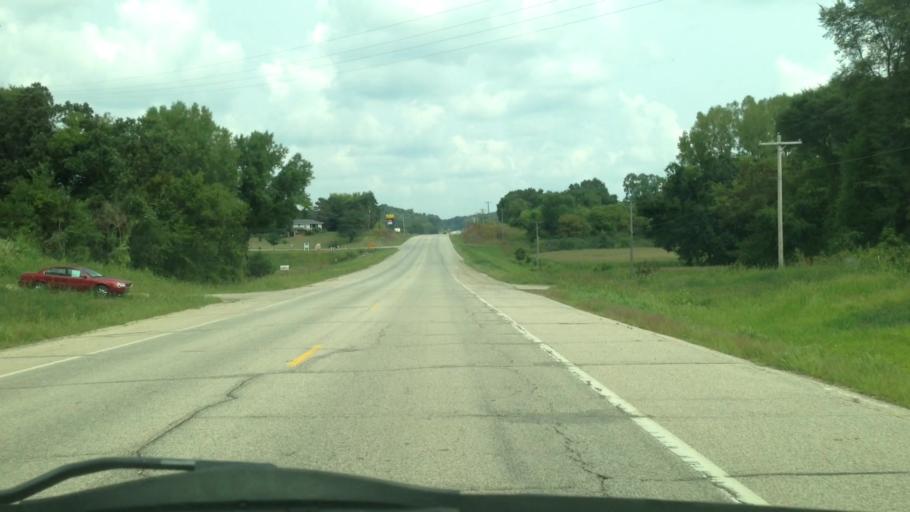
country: US
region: Minnesota
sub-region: Olmsted County
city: Rochester
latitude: 44.0977
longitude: -92.4380
